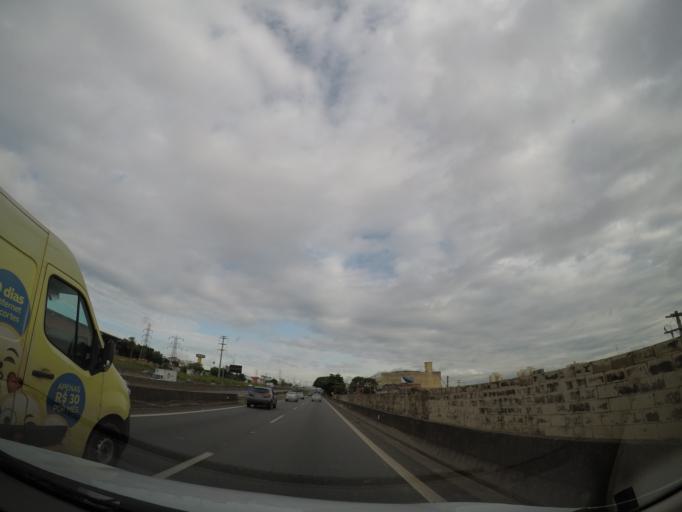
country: BR
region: Sao Paulo
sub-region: Campinas
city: Campinas
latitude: -22.9244
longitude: -47.0881
